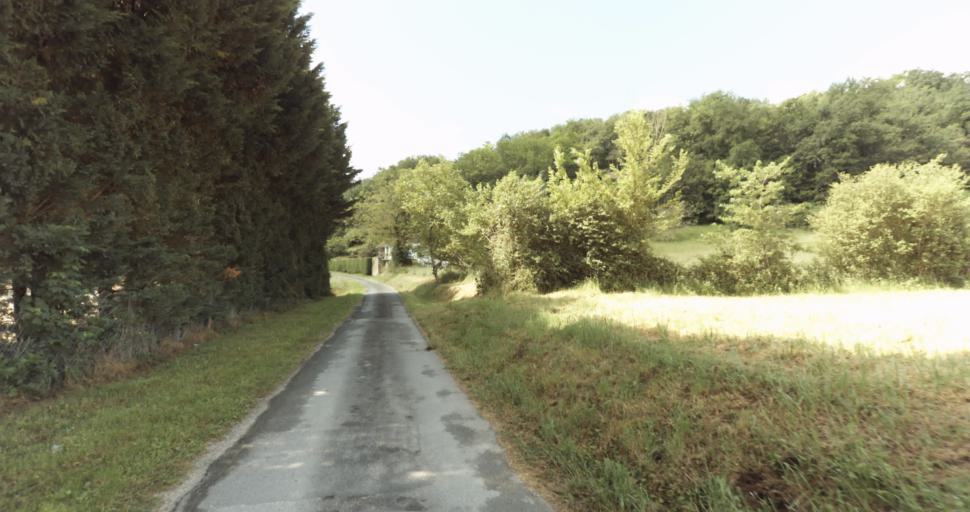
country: FR
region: Aquitaine
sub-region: Departement de la Dordogne
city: Le Bugue
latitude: 44.8479
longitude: 0.8969
